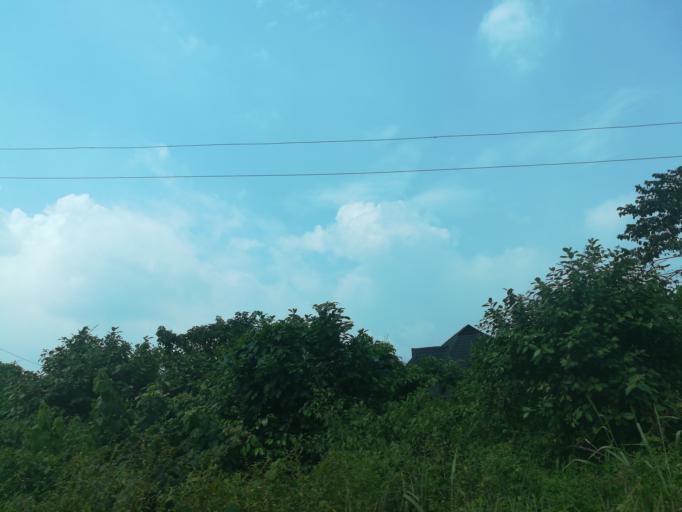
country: NG
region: Lagos
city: Ikorodu
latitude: 6.5997
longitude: 3.6270
